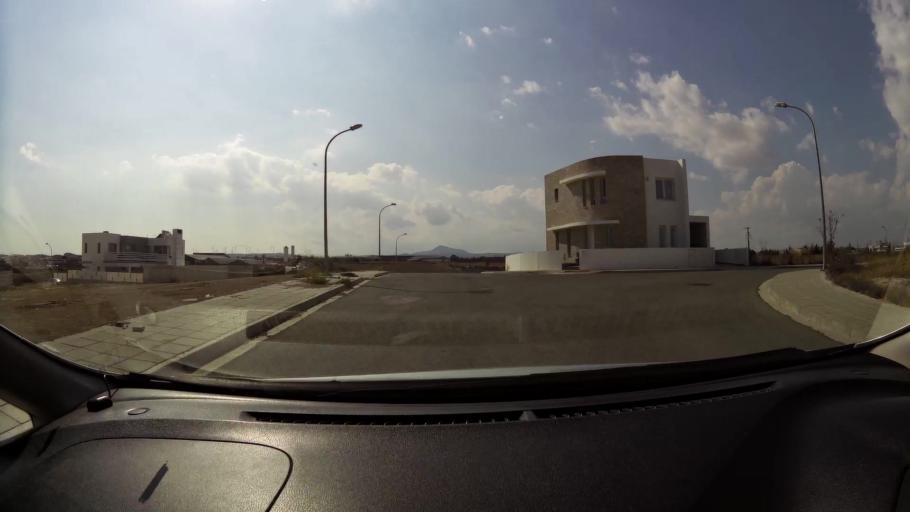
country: CY
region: Larnaka
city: Dhromolaxia
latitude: 34.9056
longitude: 33.5798
